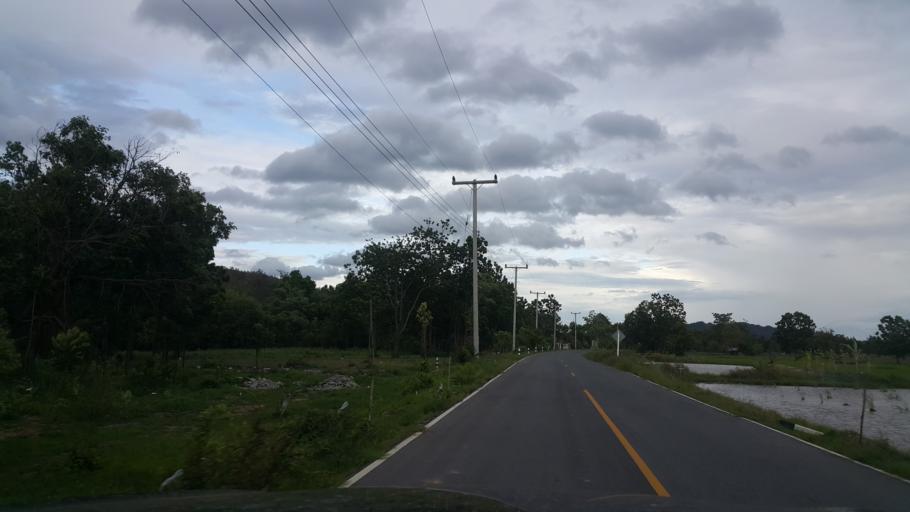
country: TH
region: Sukhothai
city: Ban Dan Lan Hoi
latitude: 17.1595
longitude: 99.5031
